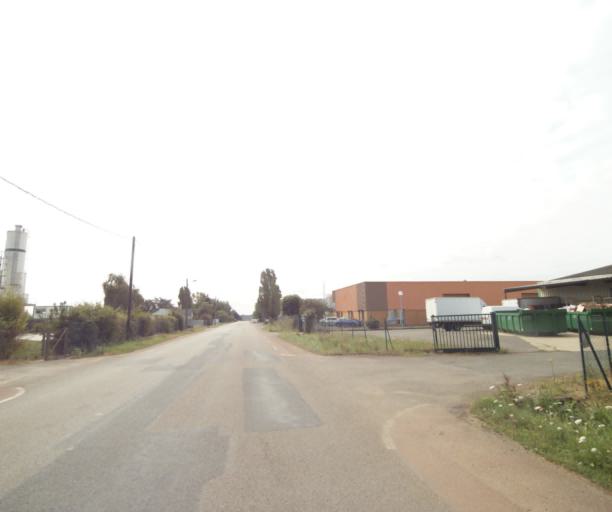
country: FR
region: Pays de la Loire
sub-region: Departement de la Sarthe
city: Sable-sur-Sarthe
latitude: 47.8240
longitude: -0.3088
